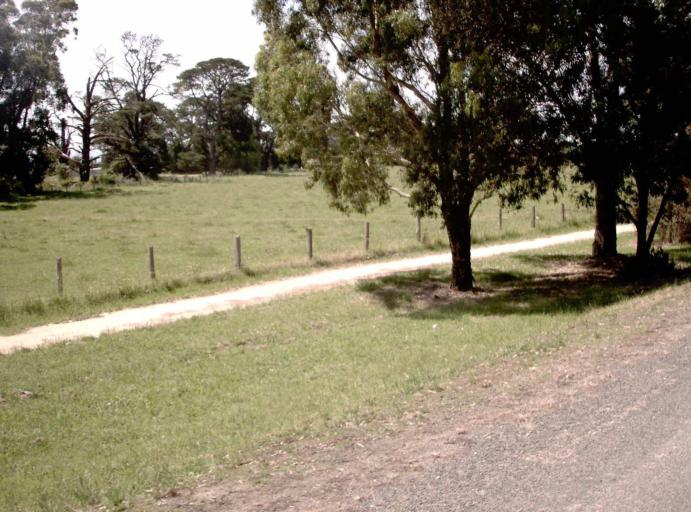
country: AU
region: Victoria
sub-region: Wellington
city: Sale
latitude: -37.9751
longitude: 147.0745
